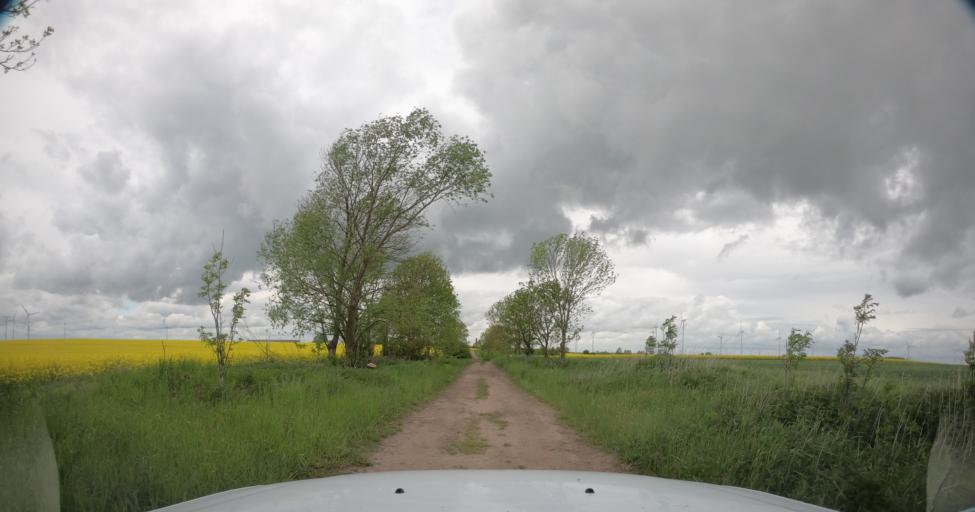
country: PL
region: West Pomeranian Voivodeship
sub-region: Powiat pyrzycki
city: Kozielice
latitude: 53.0922
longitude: 14.8152
